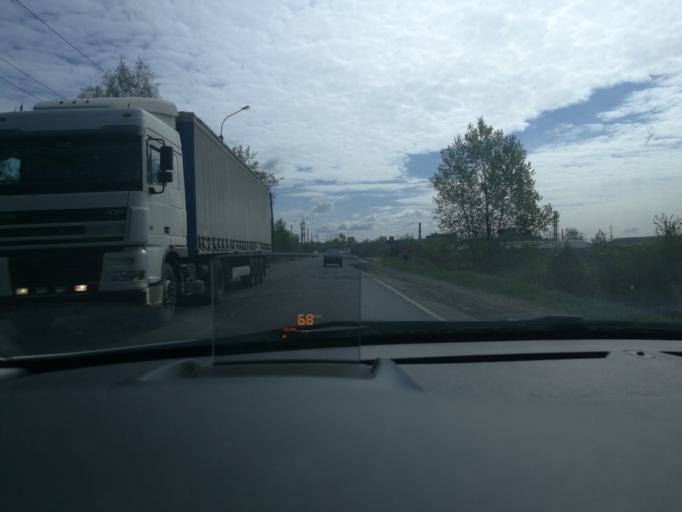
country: RU
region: Arkhangelskaya
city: Arkhangel'sk
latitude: 64.5976
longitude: 40.5345
